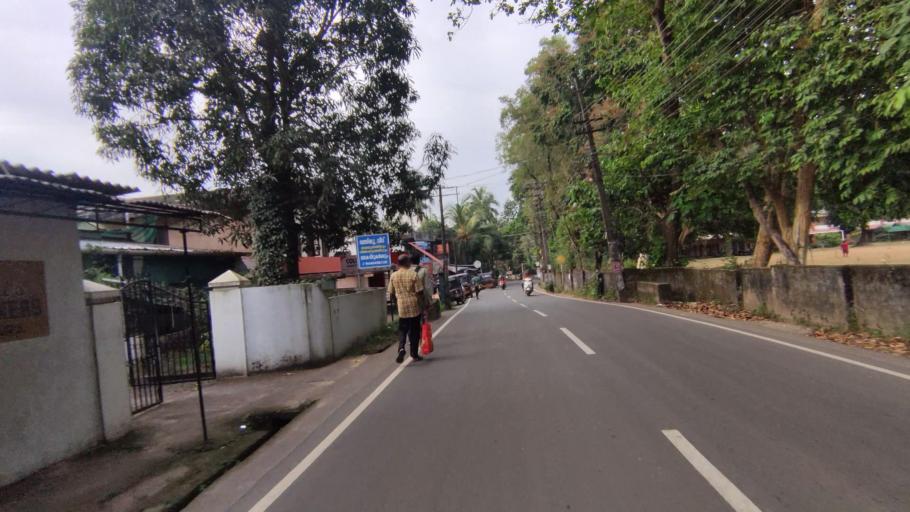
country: IN
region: Kerala
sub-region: Kottayam
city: Kottayam
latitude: 9.6324
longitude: 76.5147
